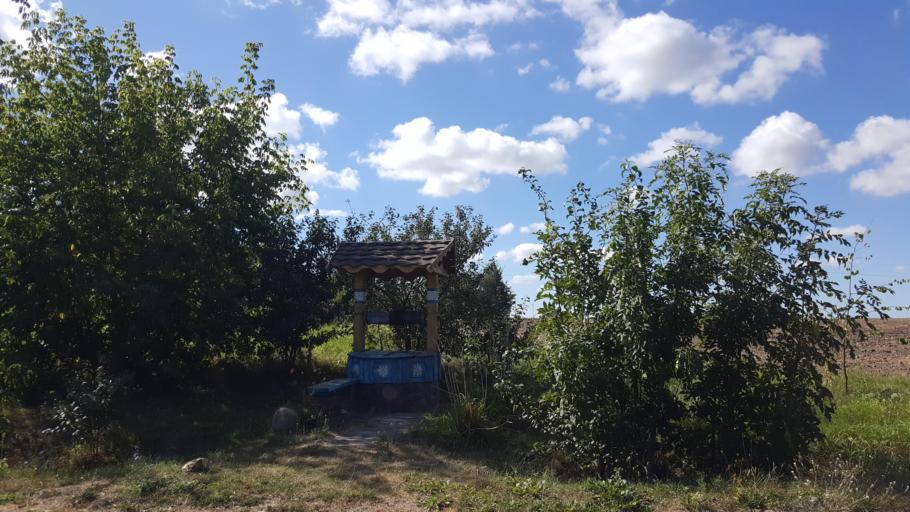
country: BY
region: Brest
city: Vysokaye
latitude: 52.3705
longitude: 23.5644
